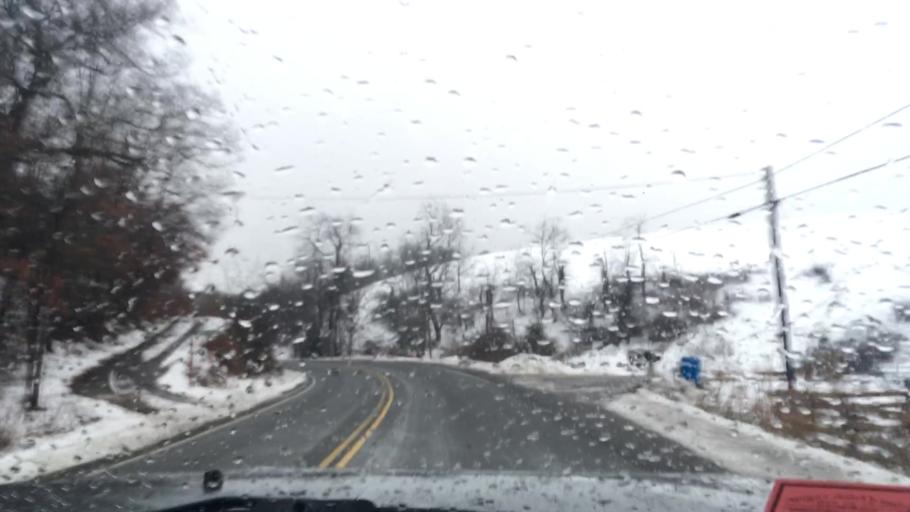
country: US
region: Virginia
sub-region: Pulaski County
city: Pulaski
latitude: 37.0237
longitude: -80.7134
